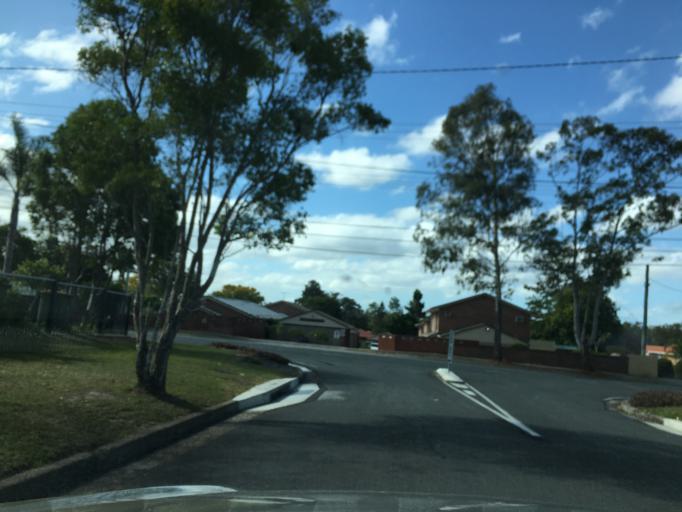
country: AU
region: Queensland
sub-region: Logan
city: Waterford West
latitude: -27.6754
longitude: 153.1272
